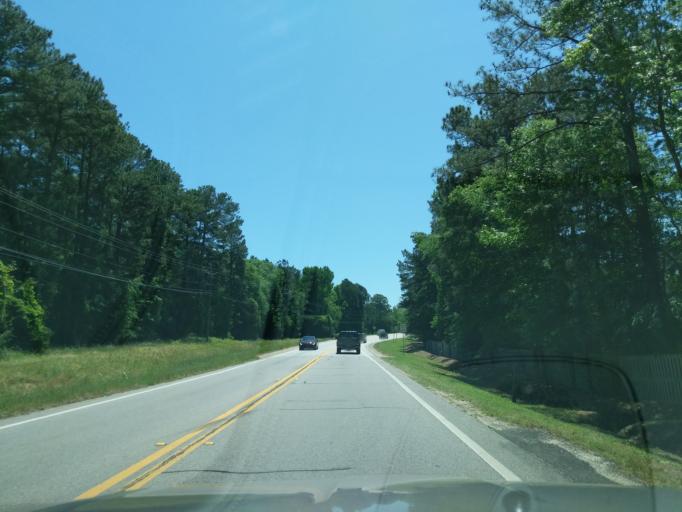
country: US
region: Georgia
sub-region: Columbia County
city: Evans
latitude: 33.5554
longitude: -82.0944
